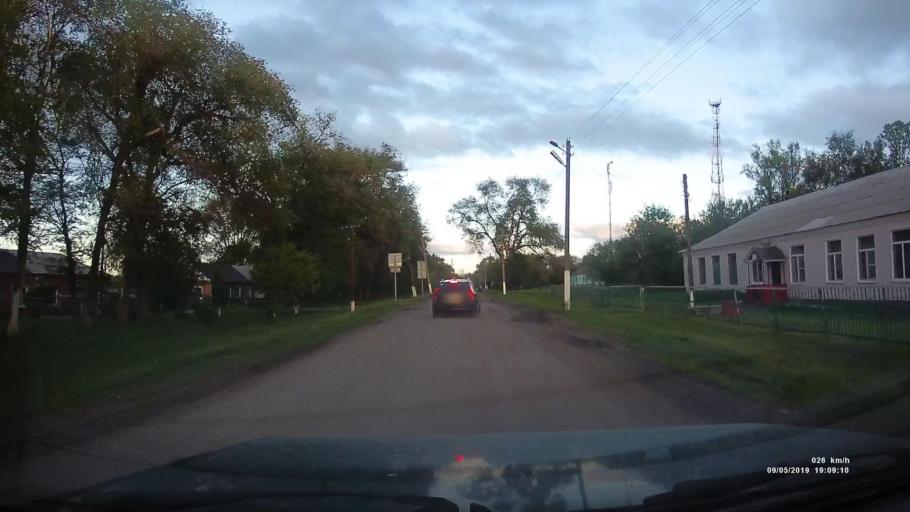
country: RU
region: Krasnodarskiy
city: Kanelovskaya
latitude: 46.7278
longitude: 39.2078
